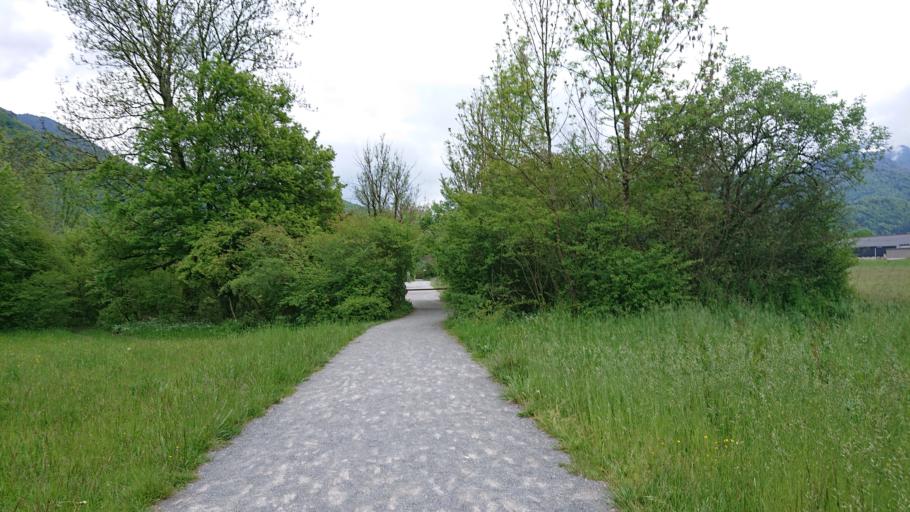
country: FR
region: Rhone-Alpes
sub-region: Departement de la Haute-Savoie
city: Doussard
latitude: 45.7859
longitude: 6.2257
